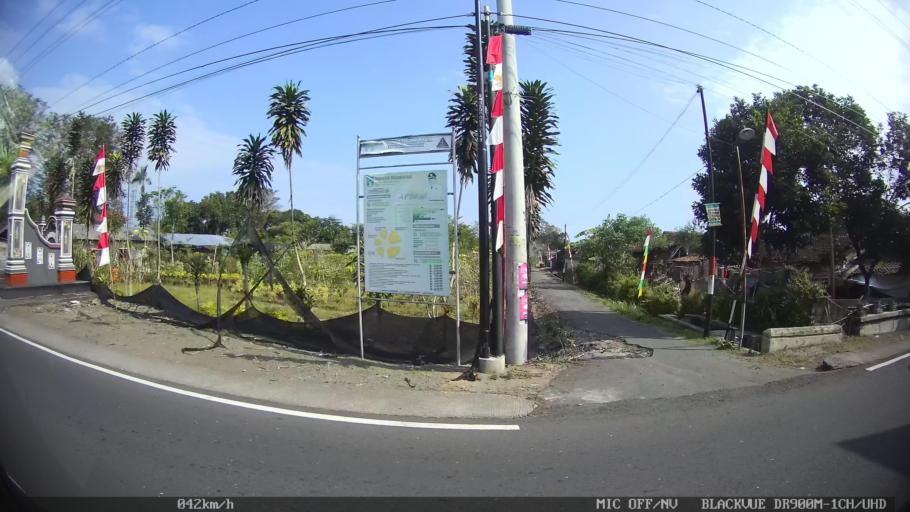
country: ID
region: Daerah Istimewa Yogyakarta
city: Depok
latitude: -7.7269
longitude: 110.4343
